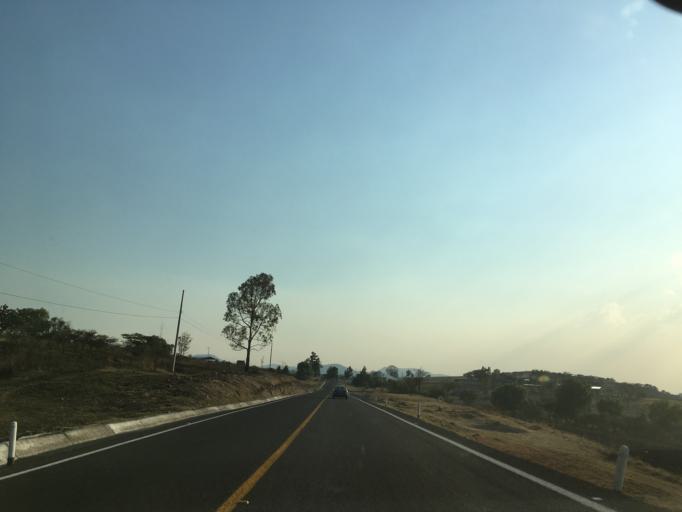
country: MX
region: Michoacan
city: Charo
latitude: 19.7620
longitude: -101.0312
